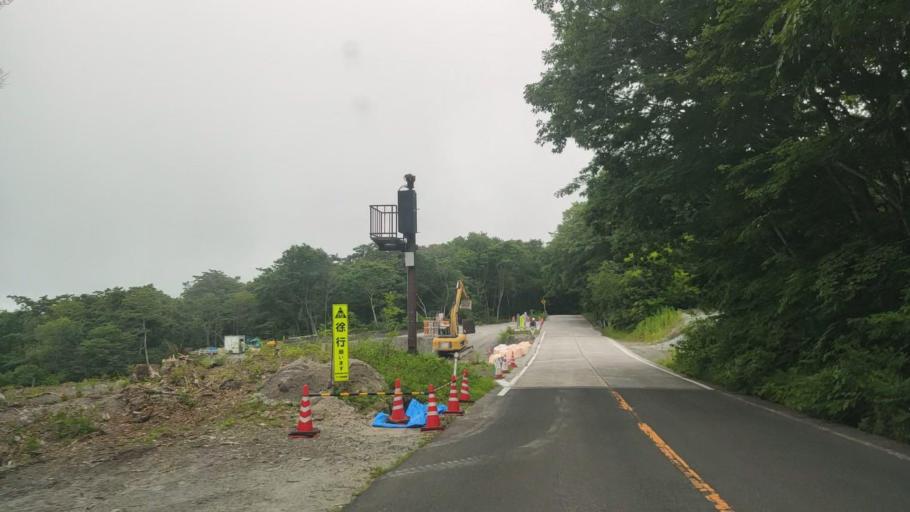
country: JP
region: Tottori
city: Yonago
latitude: 35.3550
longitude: 133.5377
